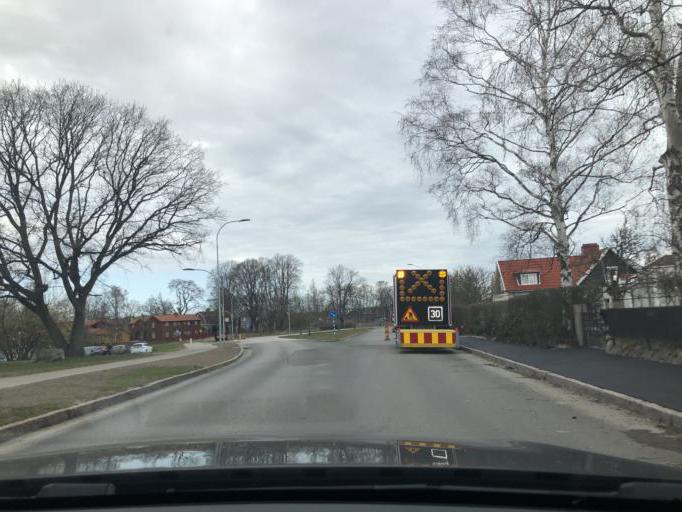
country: SE
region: Kalmar
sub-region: Kalmar Kommun
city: Kalmar
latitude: 56.6673
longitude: 16.3207
